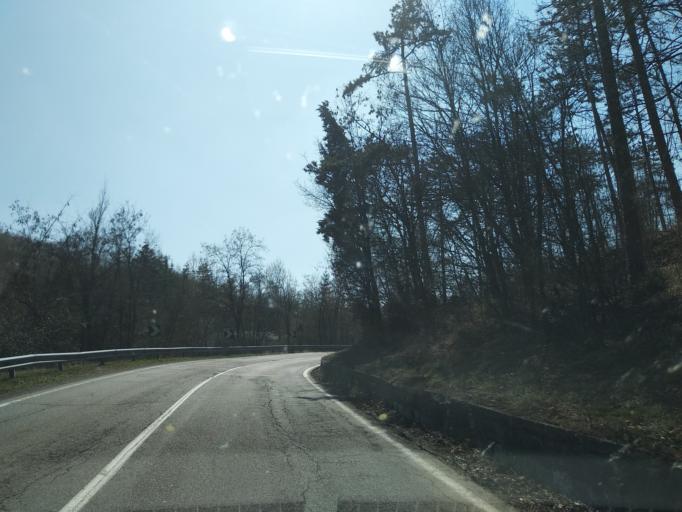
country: IT
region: Emilia-Romagna
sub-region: Provincia di Reggio Emilia
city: Vezzano sul Crostolo
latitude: 44.5805
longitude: 10.5311
